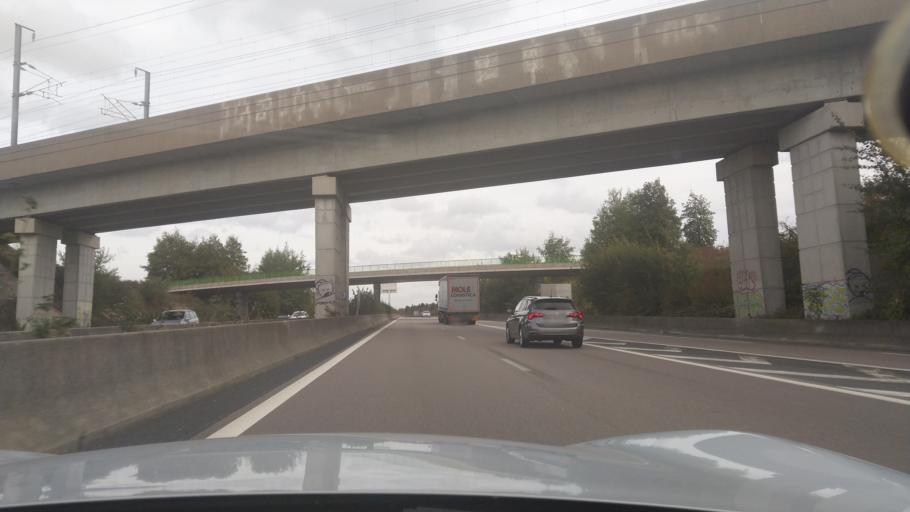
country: FR
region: Ile-de-France
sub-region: Departement du Val-d'Oise
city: Louvres
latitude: 49.0285
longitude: 2.5034
